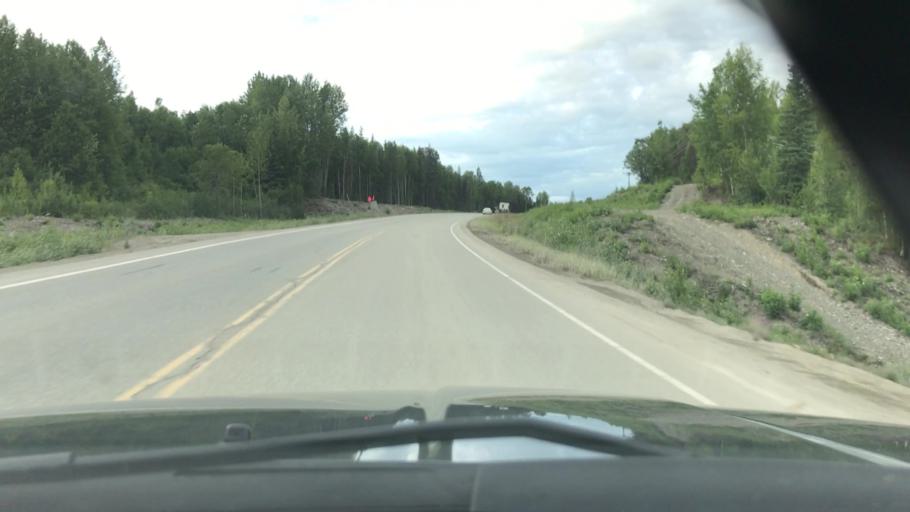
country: US
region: Alaska
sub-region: Matanuska-Susitna Borough
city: Y
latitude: 62.1066
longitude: -150.0594
